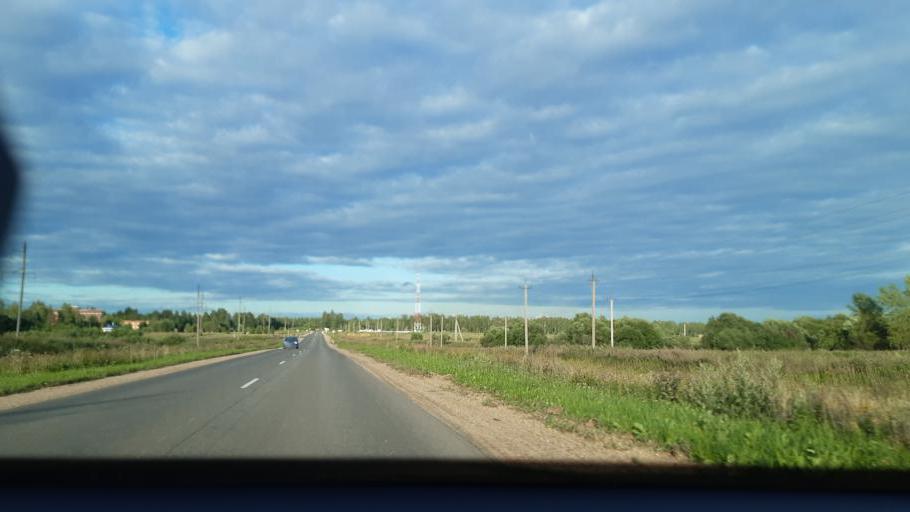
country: RU
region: Smolensk
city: Yel'nya
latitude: 54.5938
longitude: 33.1773
